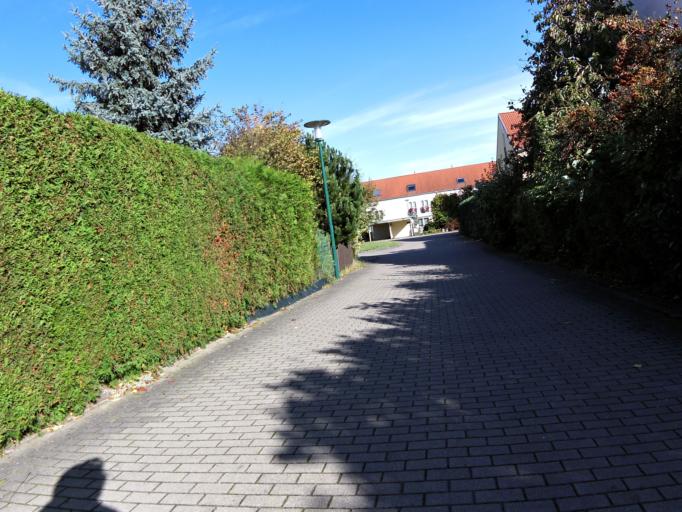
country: DE
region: Saxony
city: Grossposna
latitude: 51.3015
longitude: 12.4409
